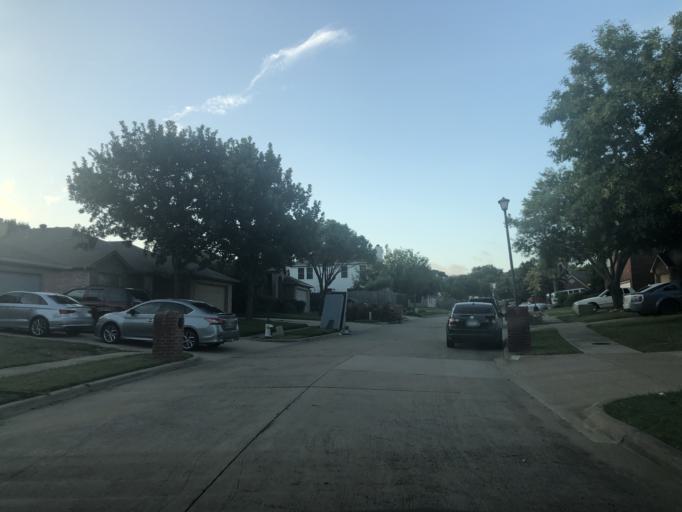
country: US
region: Texas
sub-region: Dallas County
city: Duncanville
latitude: 32.6519
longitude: -96.9713
